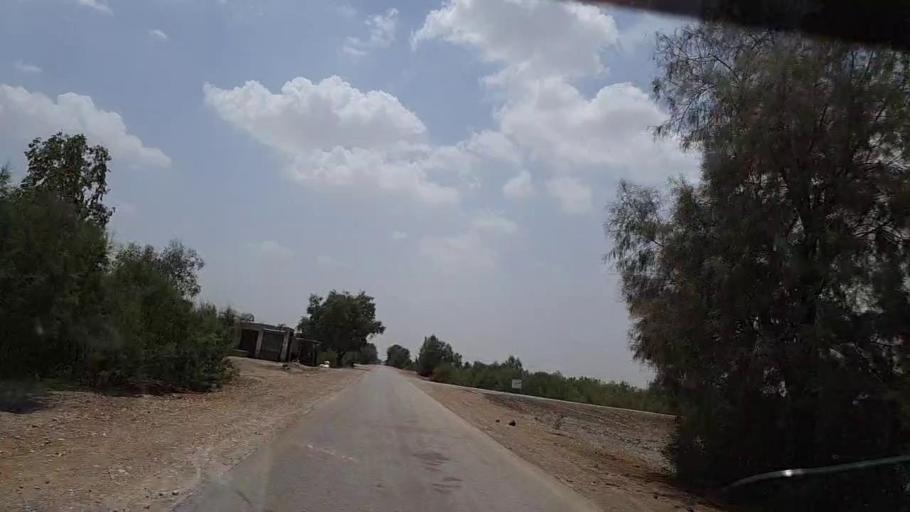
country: PK
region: Sindh
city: Bhan
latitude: 26.5411
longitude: 67.6600
